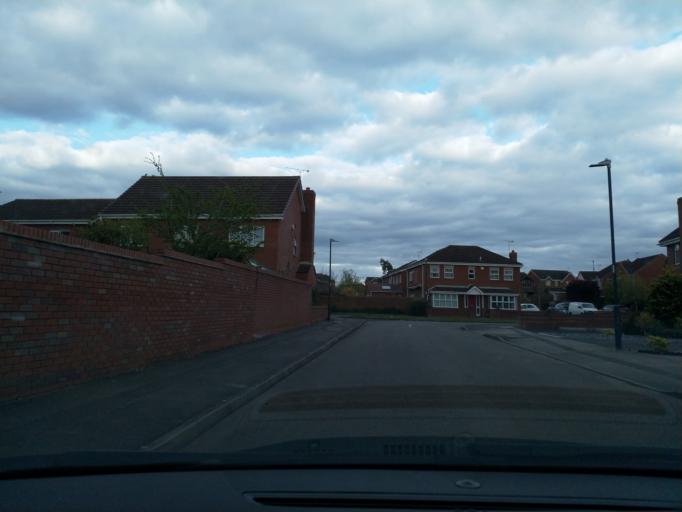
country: GB
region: England
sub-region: Warwickshire
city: Royal Leamington Spa
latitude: 52.2697
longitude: -1.5477
